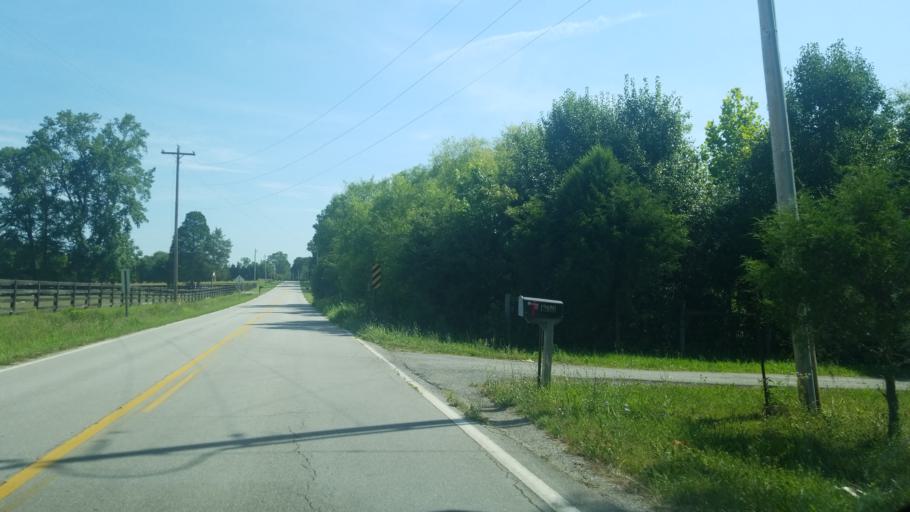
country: US
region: Tennessee
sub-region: Hamilton County
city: Sale Creek
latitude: 35.2983
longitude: -85.0384
